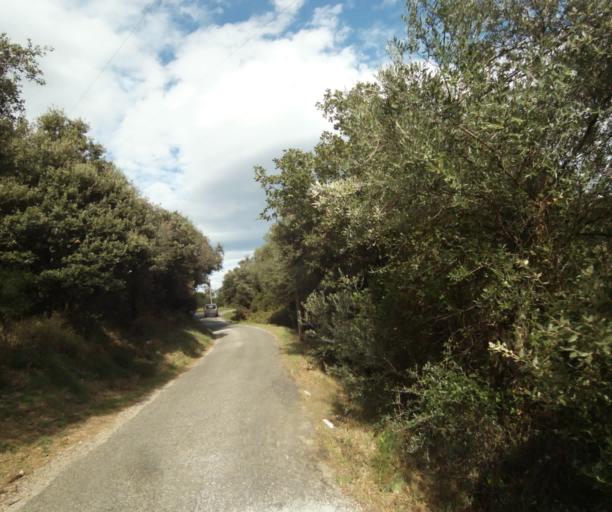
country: FR
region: Languedoc-Roussillon
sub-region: Departement des Pyrenees-Orientales
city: Sorede
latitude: 42.5258
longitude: 2.9853
